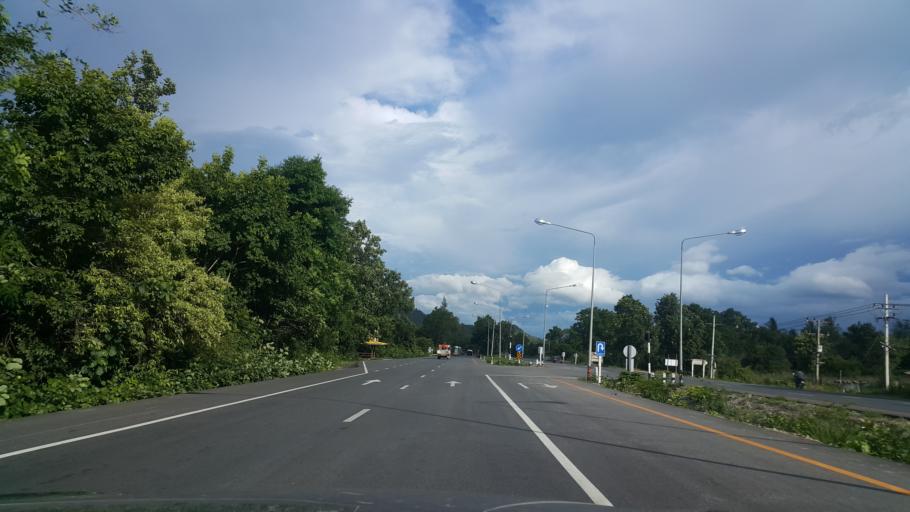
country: TH
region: Tak
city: Ban Tak
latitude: 17.0138
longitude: 99.1045
